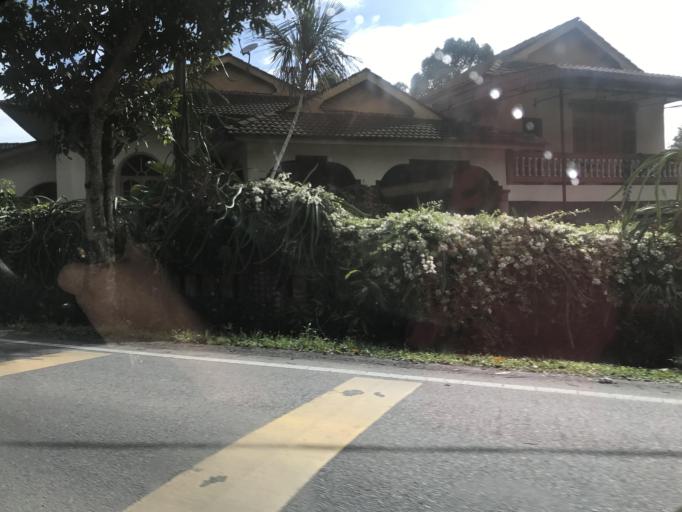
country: MY
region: Kelantan
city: Kota Bharu
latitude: 6.1235
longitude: 102.1748
